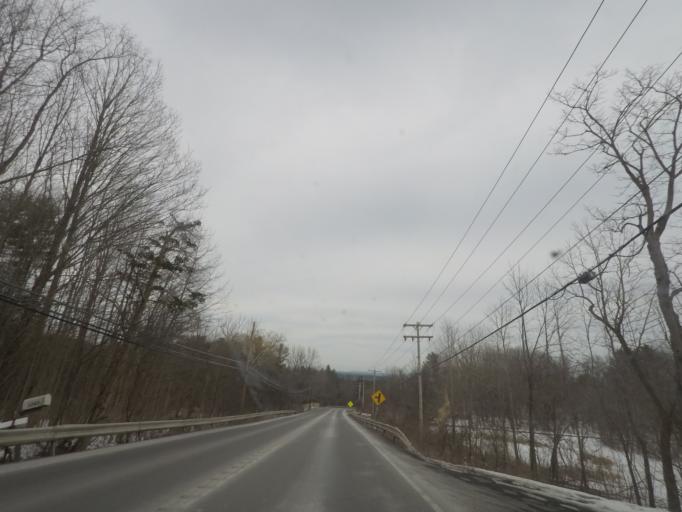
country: US
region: New York
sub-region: Albany County
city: Voorheesville
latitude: 42.5971
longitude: -73.9034
